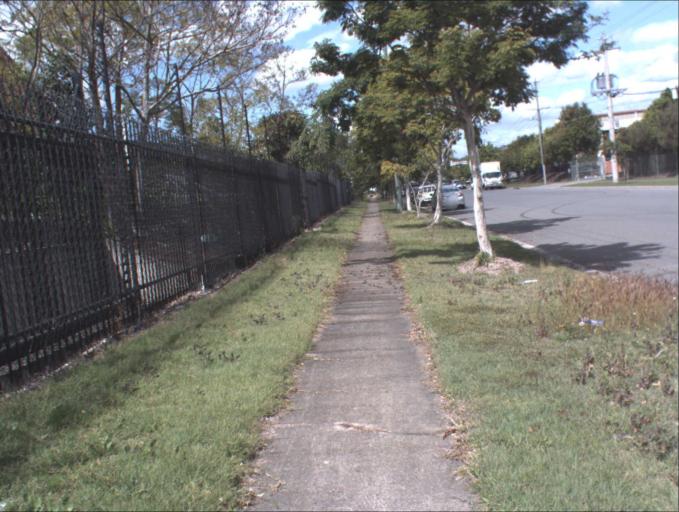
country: AU
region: Queensland
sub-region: Logan
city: Logan Reserve
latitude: -27.6806
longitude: 153.0760
